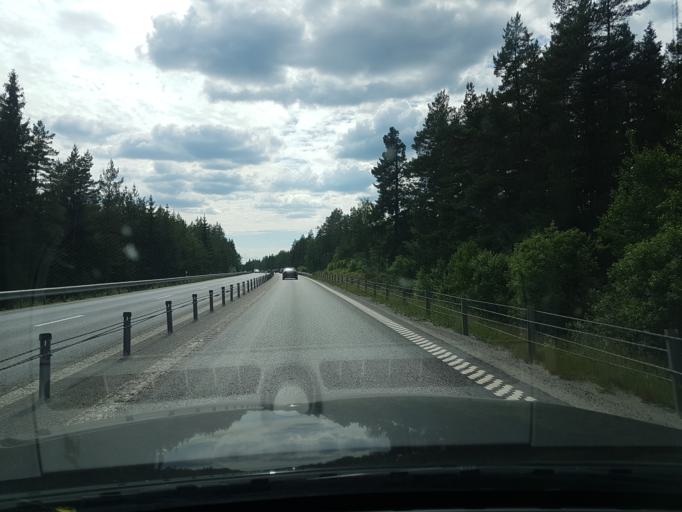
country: SE
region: Stockholm
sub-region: Osterakers Kommun
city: Akersberga
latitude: 59.6177
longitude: 18.2957
